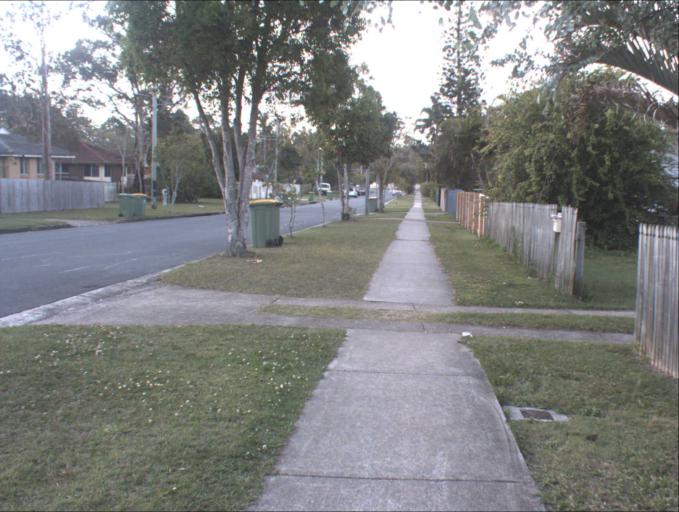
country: AU
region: Queensland
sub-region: Logan
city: Waterford West
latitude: -27.6772
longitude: 153.1291
